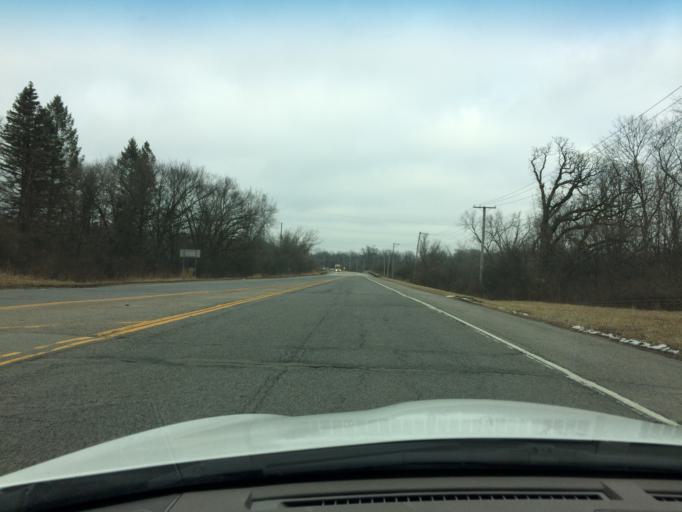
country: US
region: Illinois
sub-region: Kane County
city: Sugar Grove
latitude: 41.8026
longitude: -88.4608
